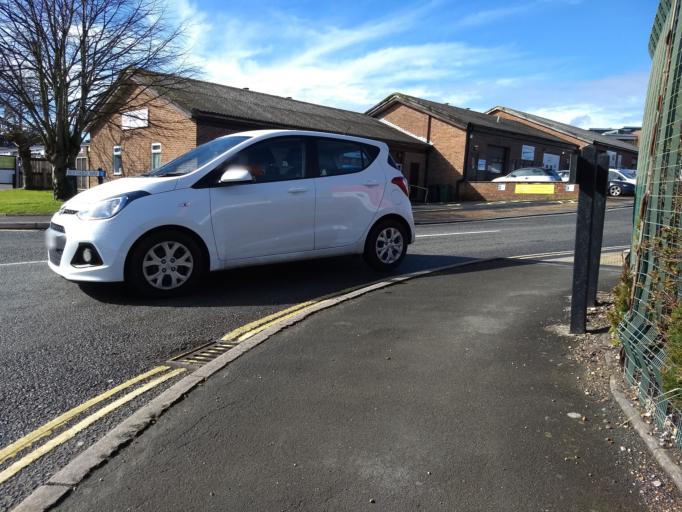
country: GB
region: England
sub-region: Isle of Wight
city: Newport
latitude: 50.7066
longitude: -1.2938
